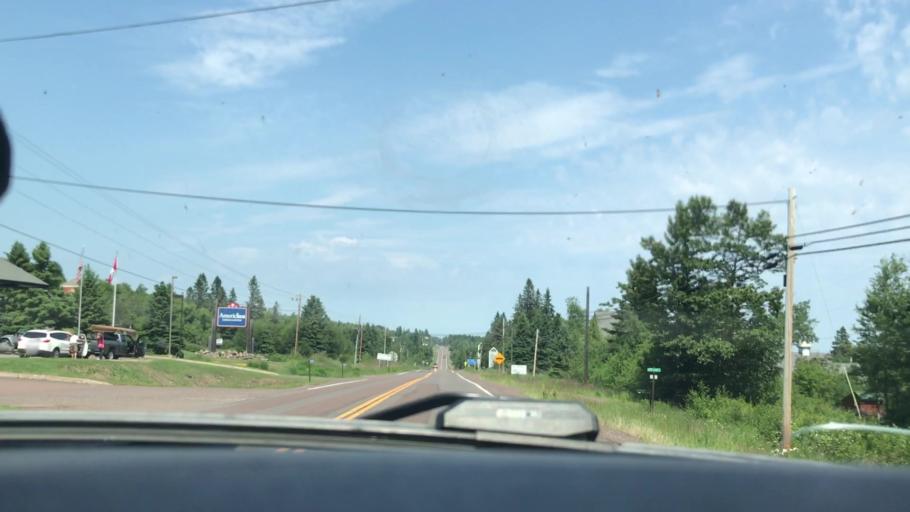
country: US
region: Minnesota
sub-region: Lake County
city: Silver Bay
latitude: 47.5720
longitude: -90.8408
